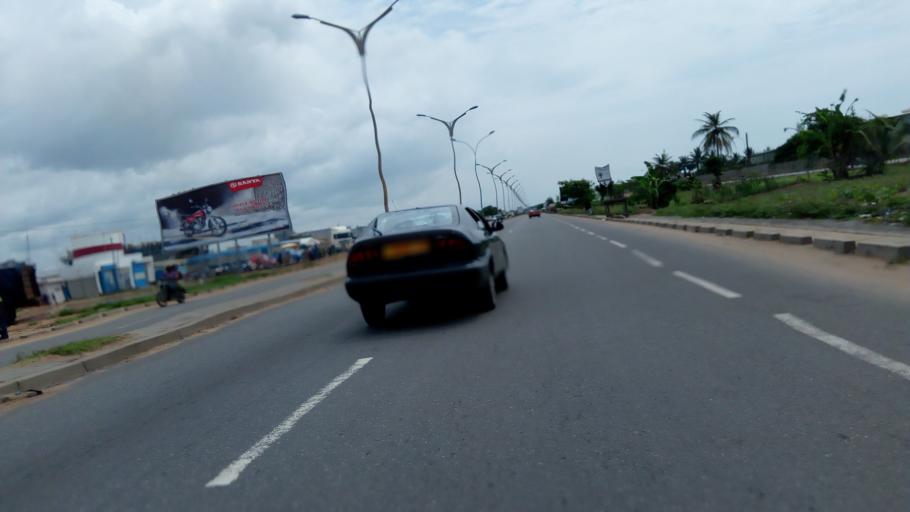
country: TG
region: Maritime
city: Lome
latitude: 6.1558
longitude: 1.3001
